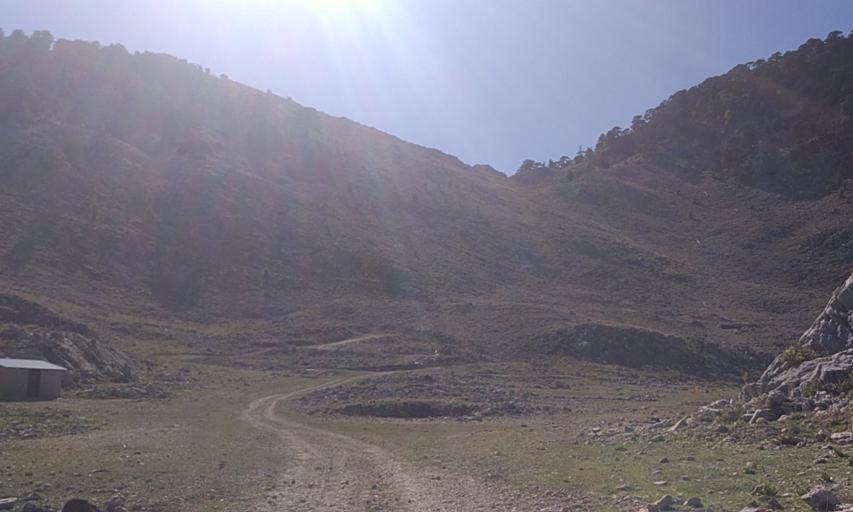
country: TR
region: Antalya
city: Altinyaka
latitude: 36.5485
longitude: 30.4114
